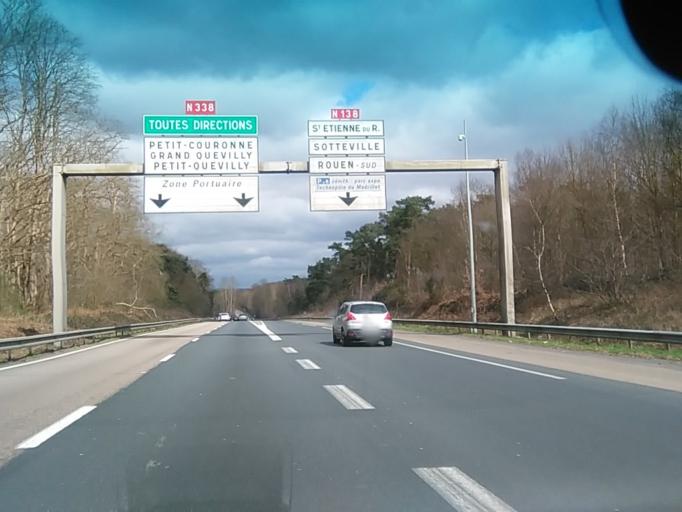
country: FR
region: Haute-Normandie
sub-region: Departement de la Seine-Maritime
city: Le Grand-Quevilly
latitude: 49.3737
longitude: 1.0454
